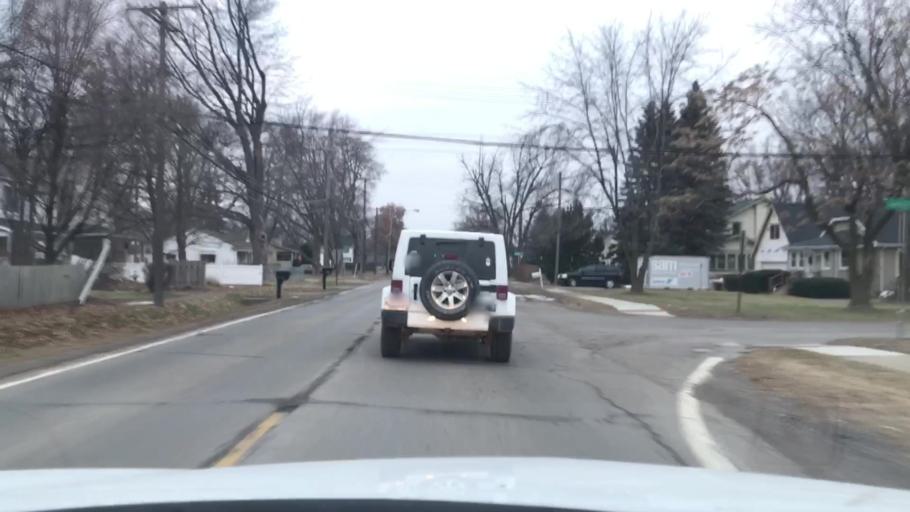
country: US
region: Michigan
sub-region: Oakland County
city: Waterford
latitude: 42.6858
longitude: -83.3734
